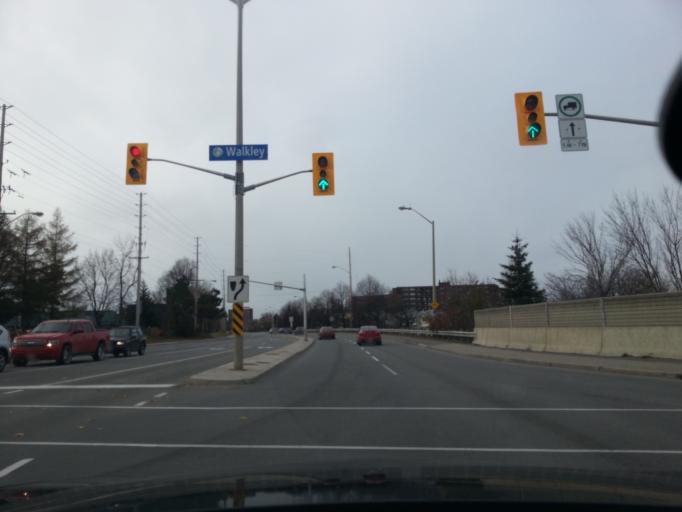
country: CA
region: Ontario
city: Ottawa
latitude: 45.3930
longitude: -75.6076
